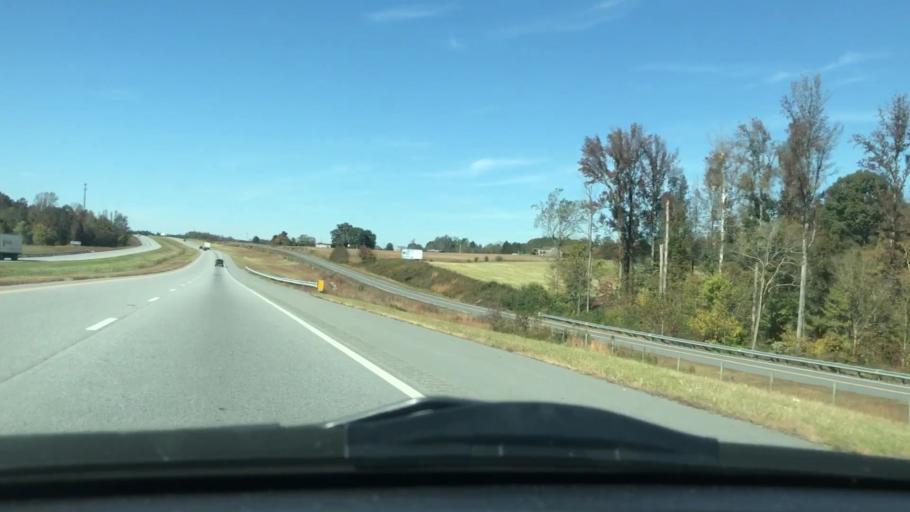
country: US
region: North Carolina
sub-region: Randolph County
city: Randleman
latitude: 35.8627
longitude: -79.8887
